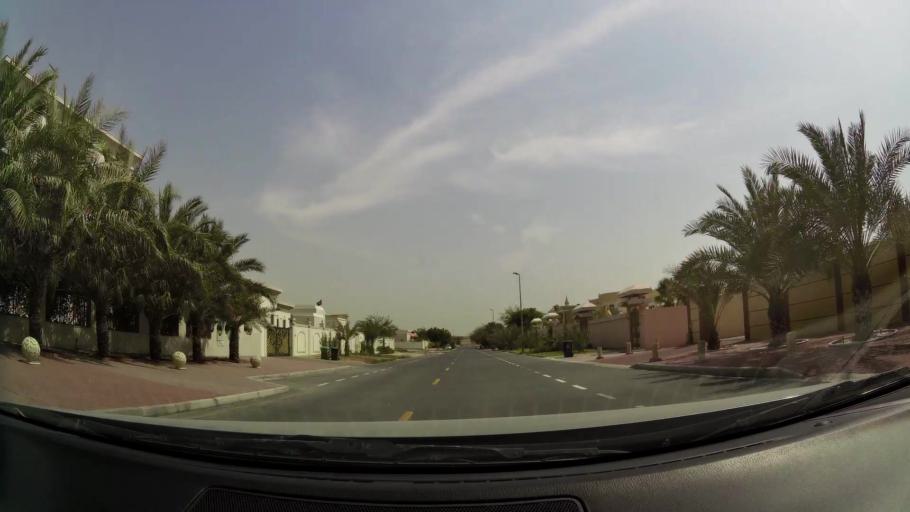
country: AE
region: Ash Shariqah
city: Sharjah
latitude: 25.2442
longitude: 55.4353
